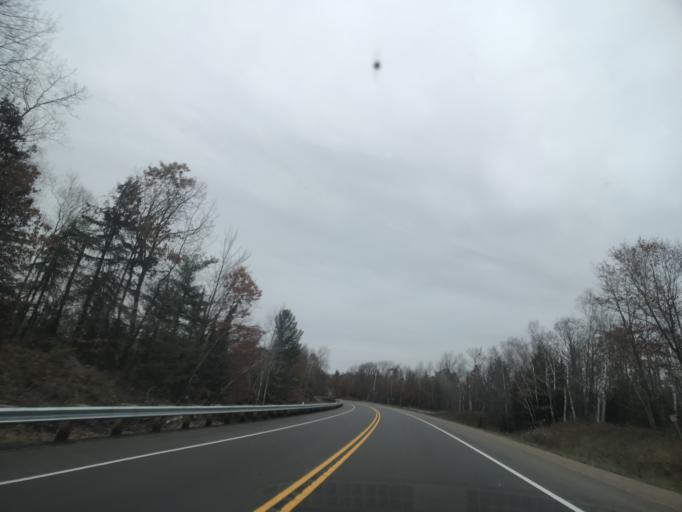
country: US
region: Wisconsin
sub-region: Menominee County
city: Legend Lake
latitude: 45.2711
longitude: -88.5088
